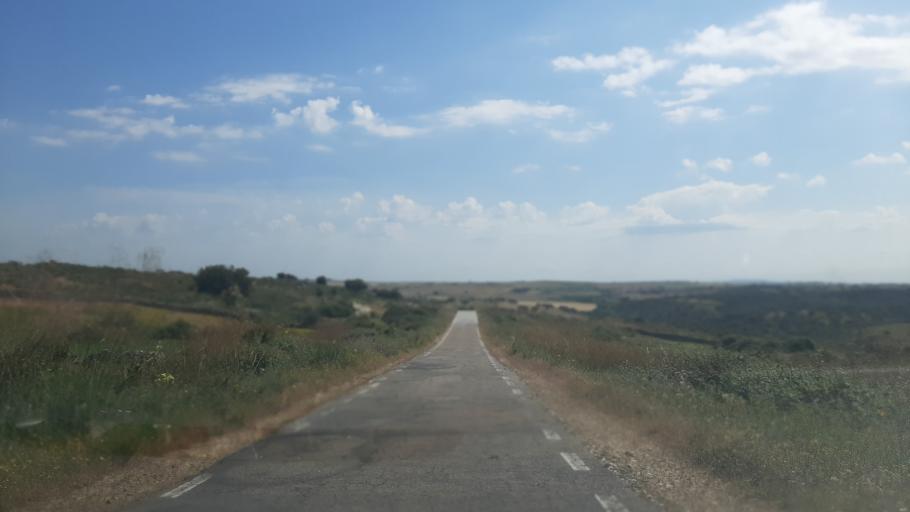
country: ES
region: Castille and Leon
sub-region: Provincia de Salamanca
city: Fuentes de Onoro
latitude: 40.6438
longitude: -6.7865
